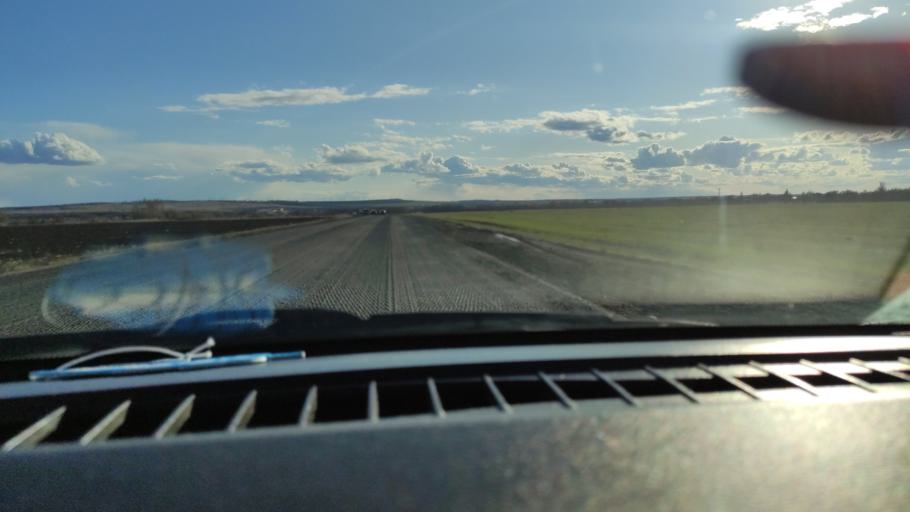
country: RU
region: Saratov
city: Yelshanka
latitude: 51.8092
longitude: 46.1988
